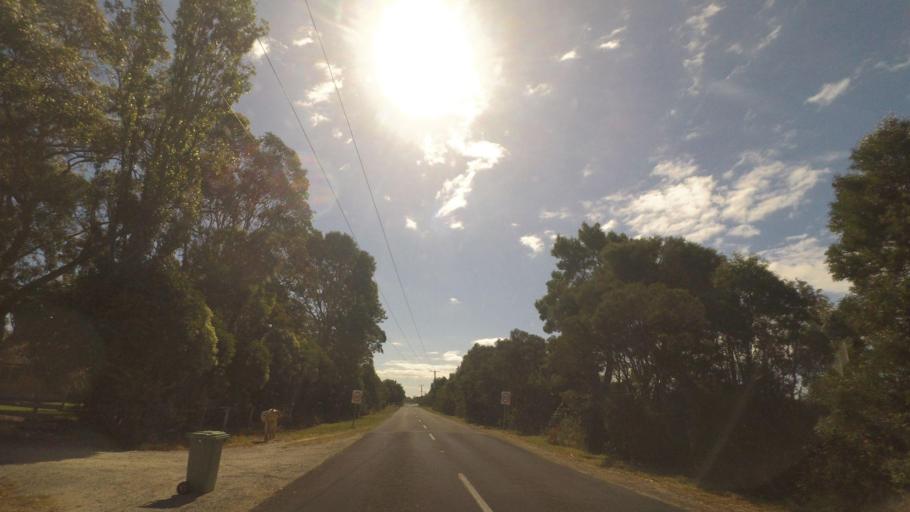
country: AU
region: Victoria
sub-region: Cardinia
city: Pakenham South
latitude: -38.1643
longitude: 145.5398
